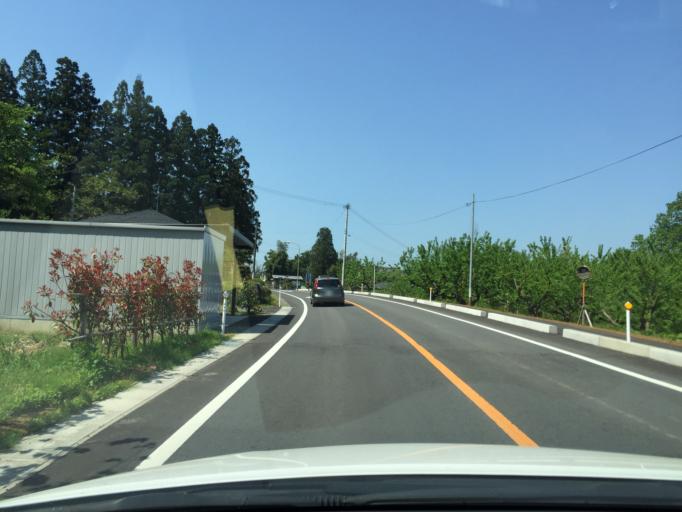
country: JP
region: Niigata
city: Muramatsu
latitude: 37.6663
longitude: 139.1405
